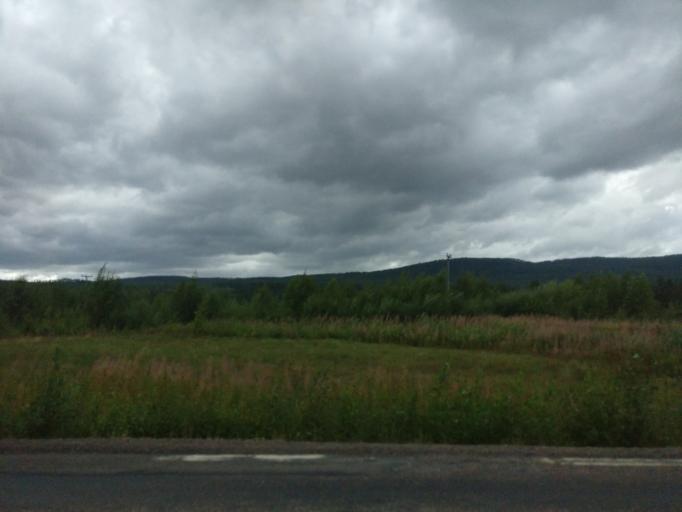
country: SE
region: Vaermland
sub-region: Torsby Kommun
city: Torsby
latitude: 60.5906
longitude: 13.0757
